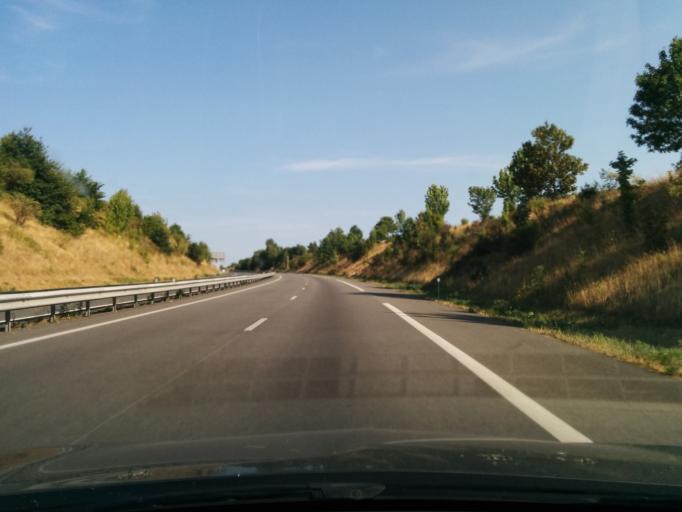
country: FR
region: Limousin
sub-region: Departement de la Haute-Vienne
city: Pierre-Buffiere
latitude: 45.6802
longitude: 1.3698
